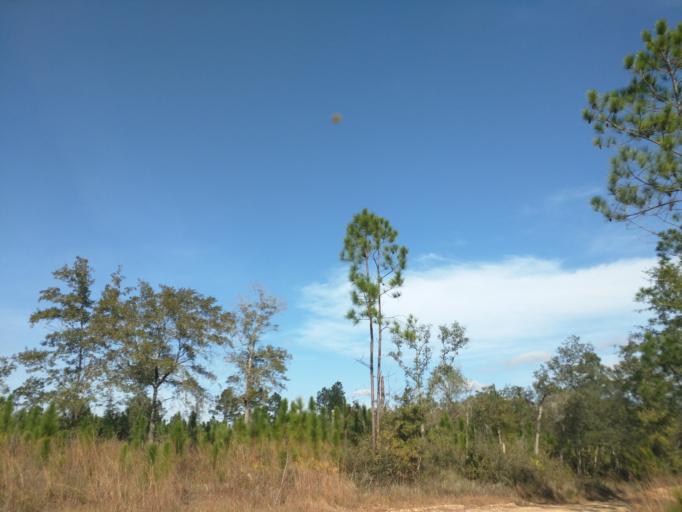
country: US
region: Florida
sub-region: Escambia County
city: Cantonment
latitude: 30.5487
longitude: -87.4294
